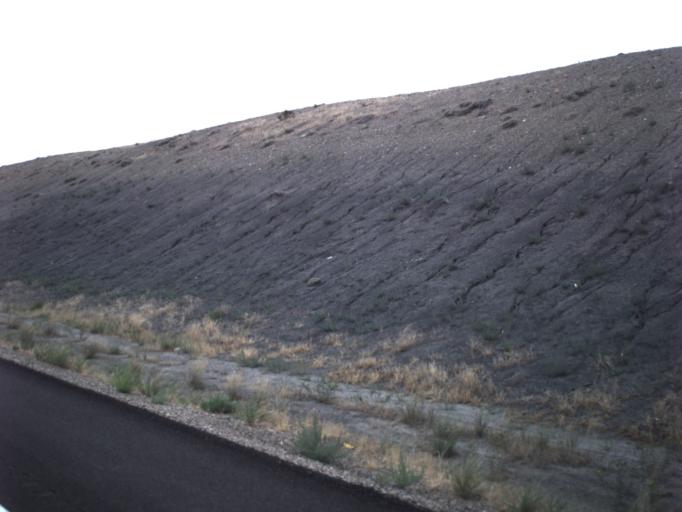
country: US
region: Utah
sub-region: Carbon County
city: East Carbon City
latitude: 39.0866
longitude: -110.3195
